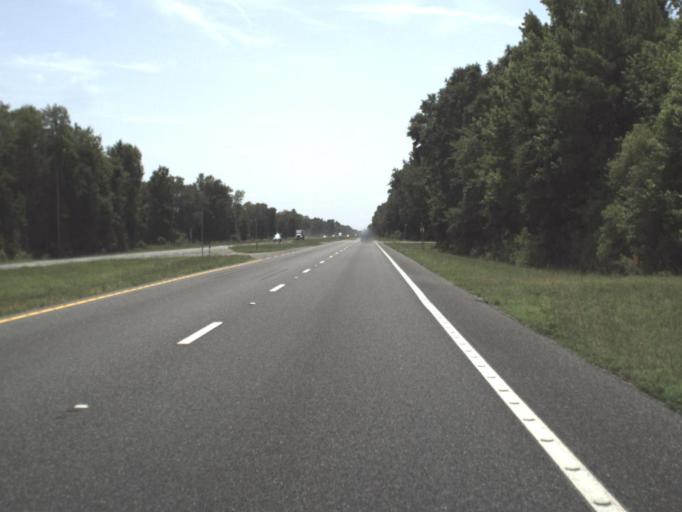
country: US
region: Florida
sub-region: Taylor County
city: Steinhatchee
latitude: 29.9140
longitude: -83.4324
